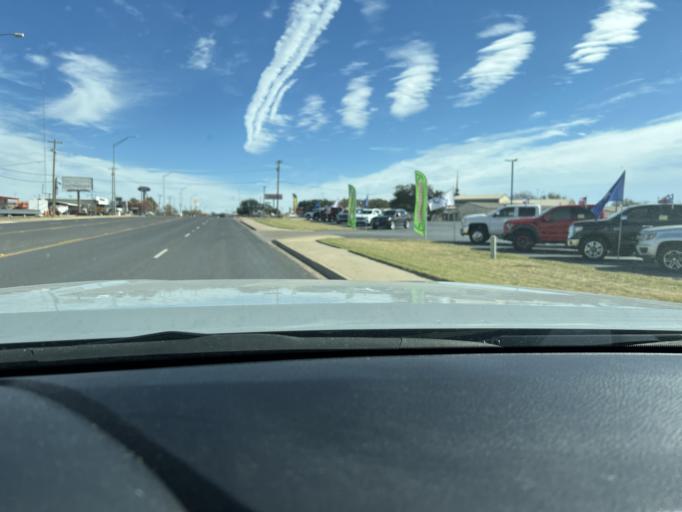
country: US
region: Texas
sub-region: Eastland County
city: Eastland
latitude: 32.4016
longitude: -98.7998
